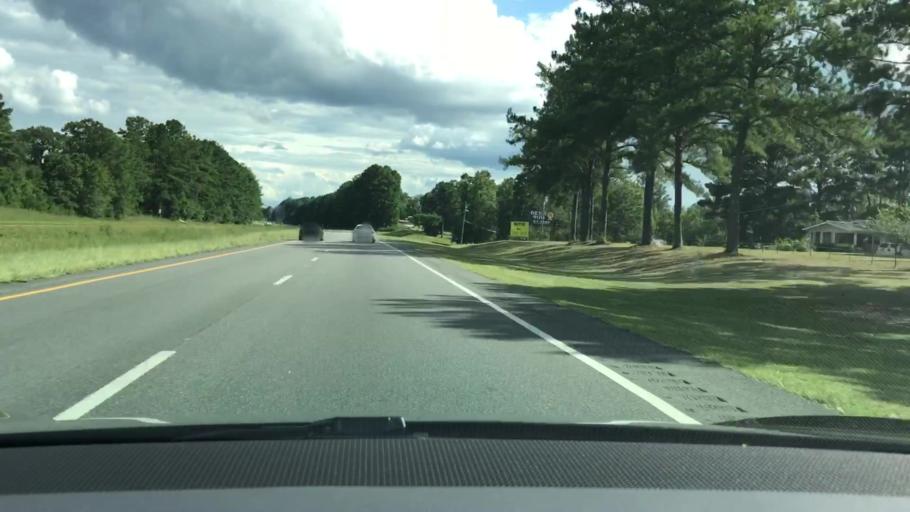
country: US
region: Alabama
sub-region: Pike County
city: Troy
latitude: 31.8973
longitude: -86.0104
